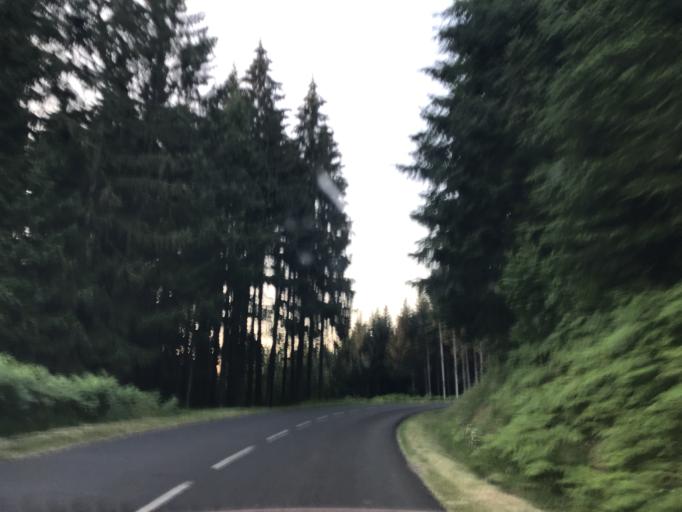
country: FR
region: Auvergne
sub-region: Departement du Puy-de-Dome
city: Celles-sur-Durolle
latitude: 45.7592
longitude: 3.6684
